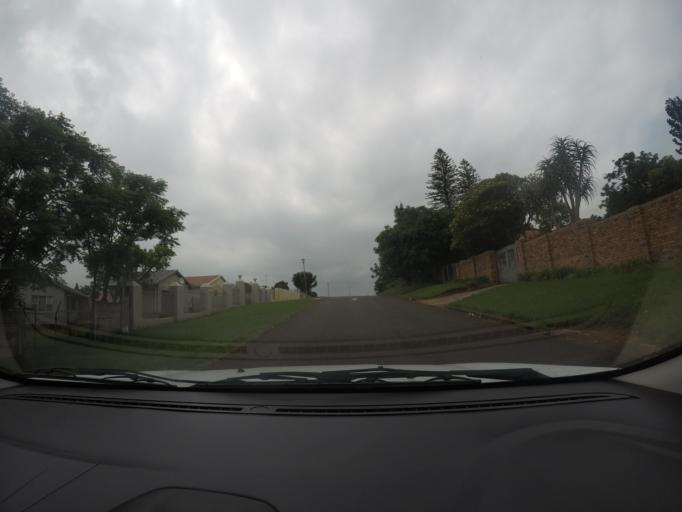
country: ZA
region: KwaZulu-Natal
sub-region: uThungulu District Municipality
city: Empangeni
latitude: -28.7380
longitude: 31.8992
